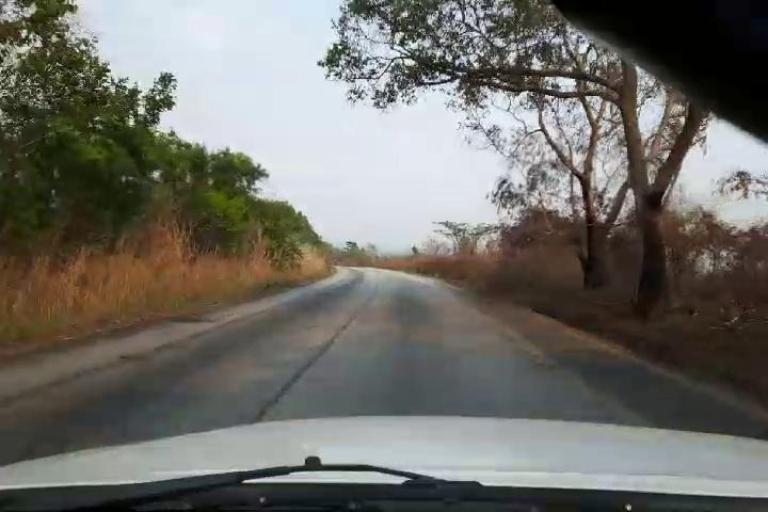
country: SL
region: Southern Province
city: Baiima
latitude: 8.1699
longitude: -11.9501
